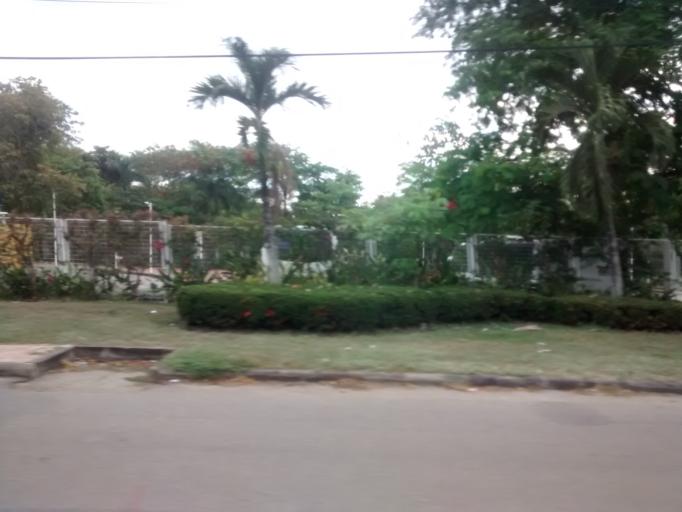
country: CO
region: Tolima
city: Melgar
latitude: 4.2256
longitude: -74.6985
